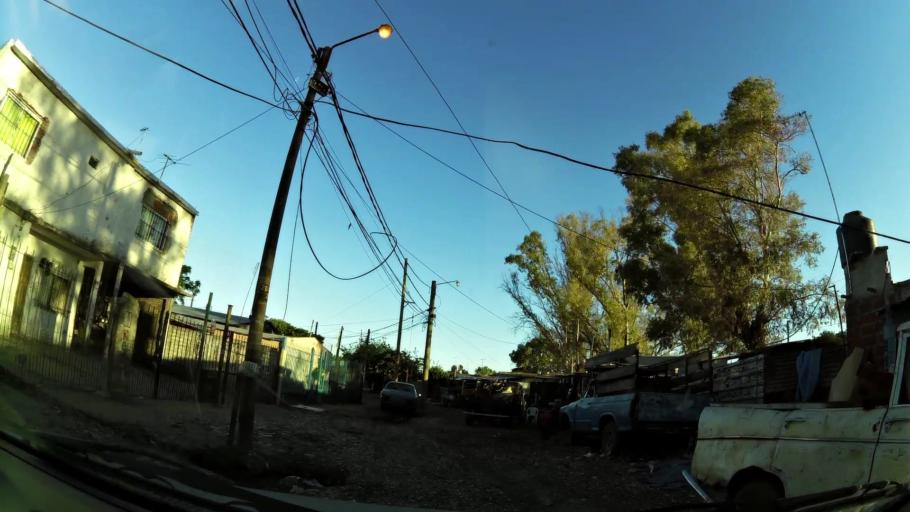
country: AR
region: Buenos Aires
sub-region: Partido de Almirante Brown
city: Adrogue
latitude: -34.7816
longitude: -58.3373
